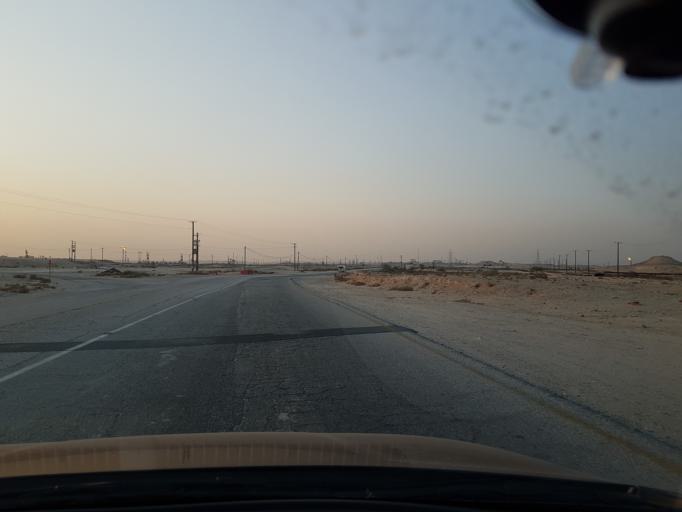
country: BH
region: Central Governorate
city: Dar Kulayb
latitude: 26.0563
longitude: 50.5552
